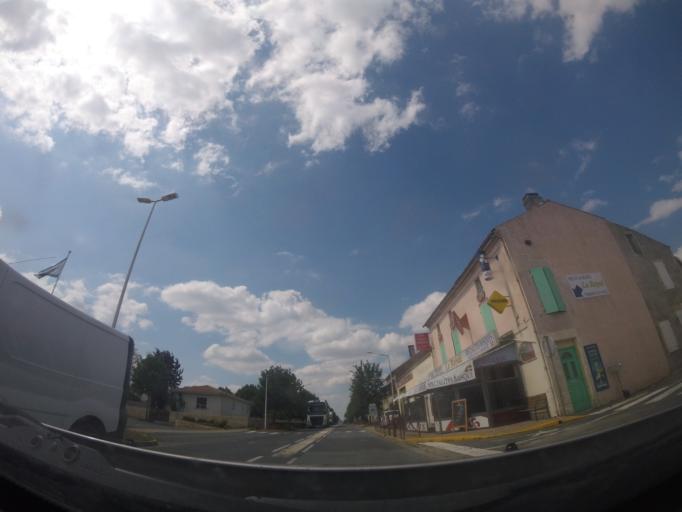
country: FR
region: Poitou-Charentes
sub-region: Departement de la Charente-Maritime
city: Bords
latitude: 45.8612
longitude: -0.8374
